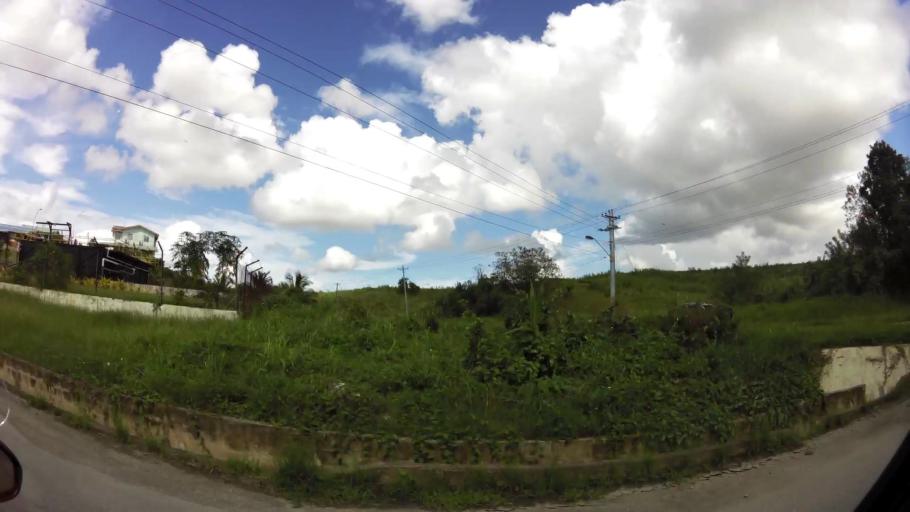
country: TT
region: Penal/Debe
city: Debe
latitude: 10.2403
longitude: -61.4380
